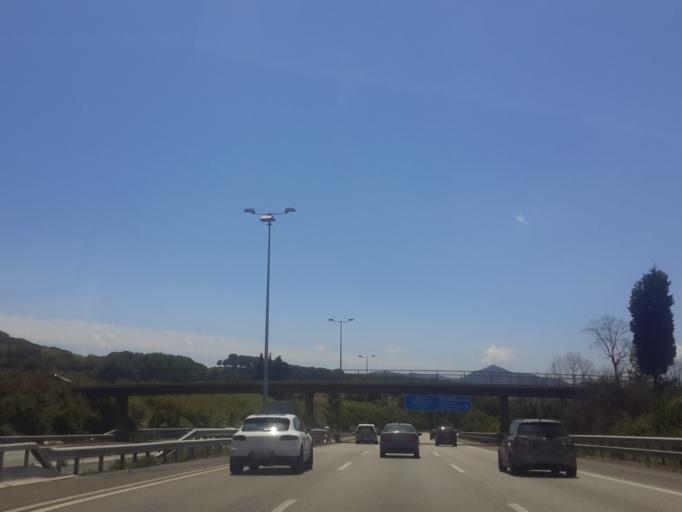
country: ES
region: Catalonia
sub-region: Provincia de Barcelona
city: Granollers
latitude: 41.5748
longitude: 2.2847
